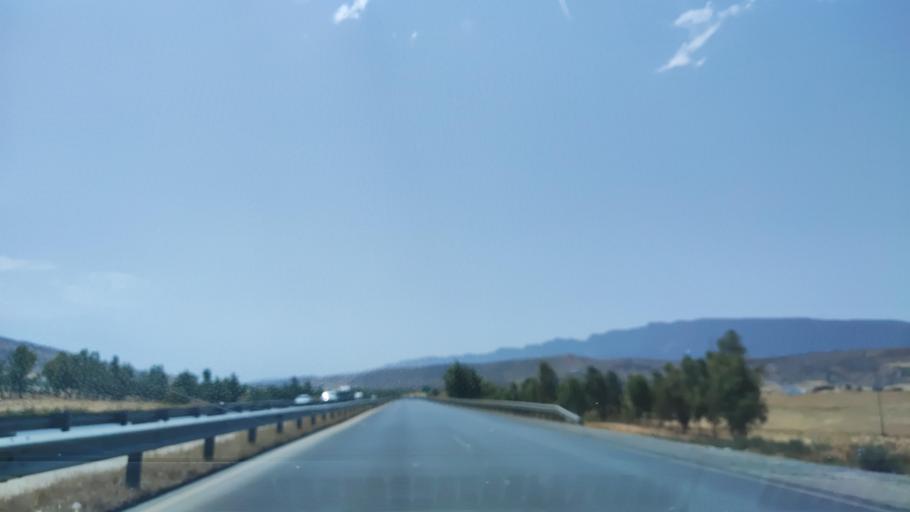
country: IQ
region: Arbil
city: Shaqlawah
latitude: 36.4620
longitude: 44.3836
